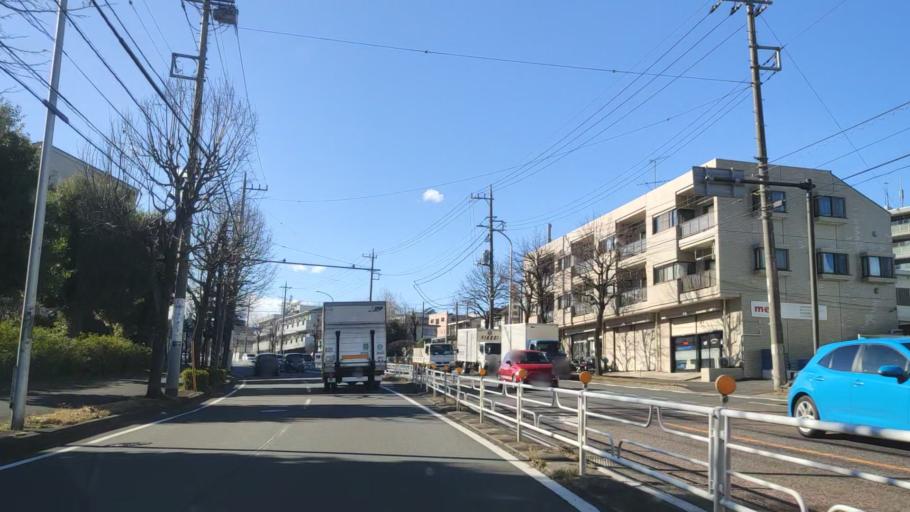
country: JP
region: Tokyo
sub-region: Machida-shi
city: Machida
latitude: 35.5238
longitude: 139.5211
